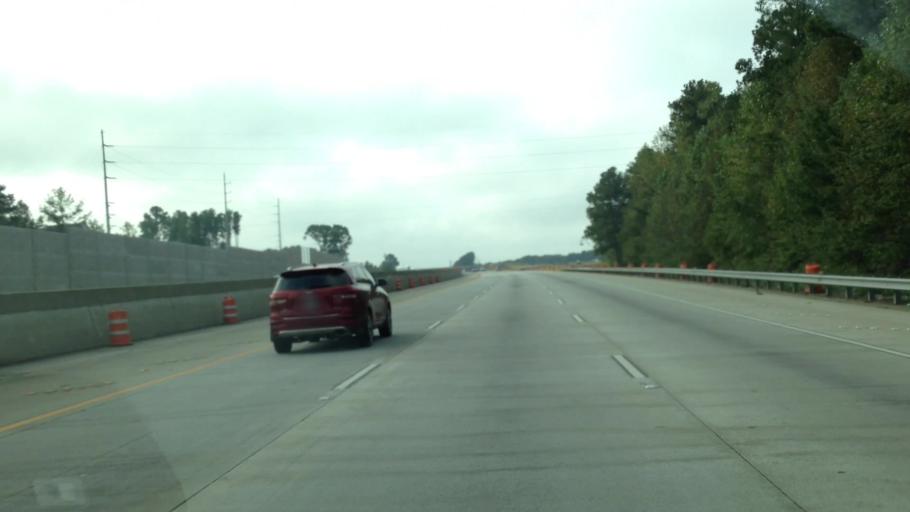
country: US
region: Georgia
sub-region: Coweta County
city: East Newnan
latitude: 33.3677
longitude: -84.7596
